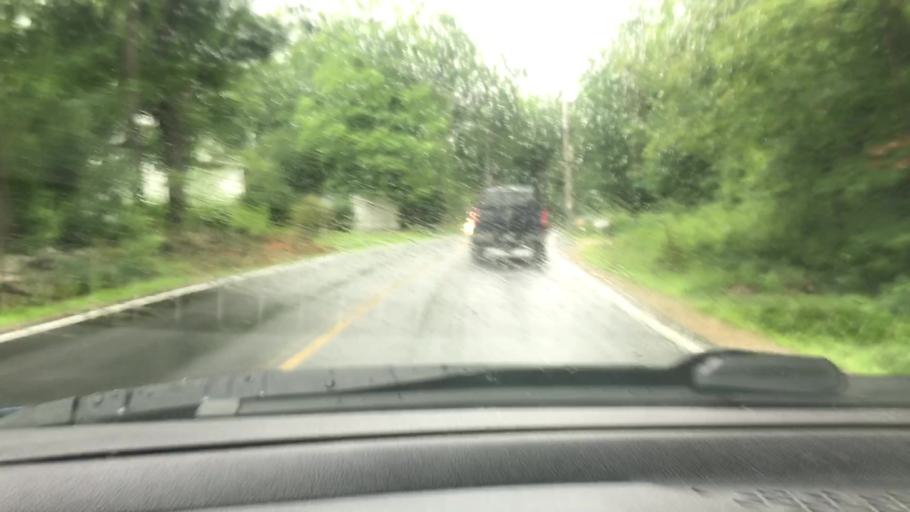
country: US
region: New Hampshire
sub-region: Rockingham County
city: Candia
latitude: 43.1654
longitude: -71.2459
